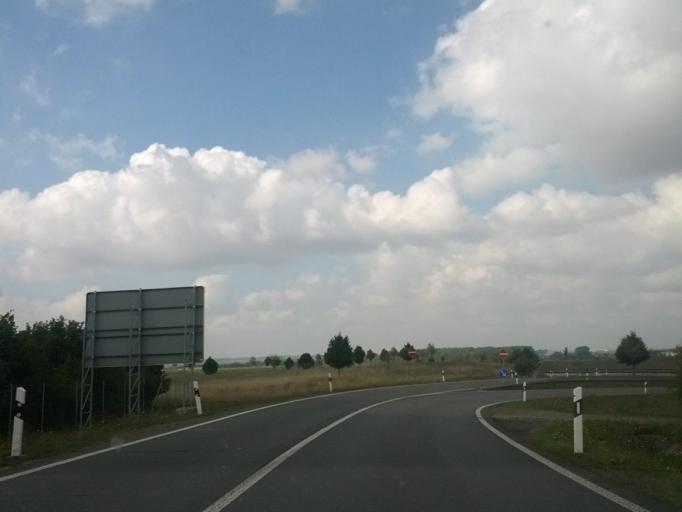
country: DE
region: Thuringia
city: Ingersleben
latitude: 50.9558
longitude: 10.9386
